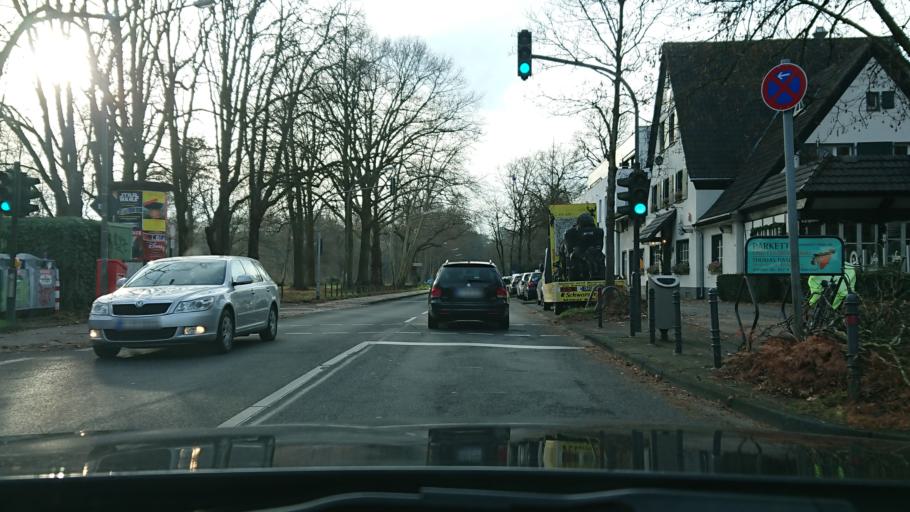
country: DE
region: North Rhine-Westphalia
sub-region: Regierungsbezirk Koln
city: Neustadt/Sued
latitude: 50.9170
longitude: 6.9000
